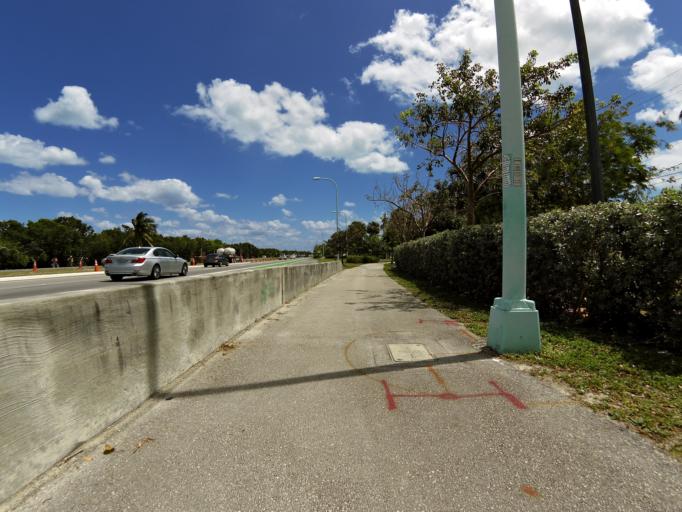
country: US
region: Florida
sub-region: Miami-Dade County
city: Key Biscayne
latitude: 25.7274
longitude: -80.1556
